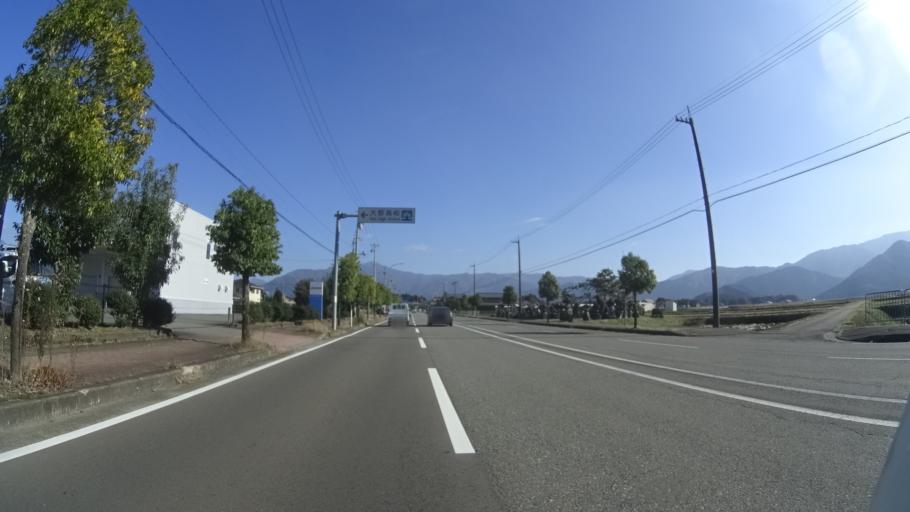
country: JP
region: Fukui
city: Ono
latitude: 35.9716
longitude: 136.4840
